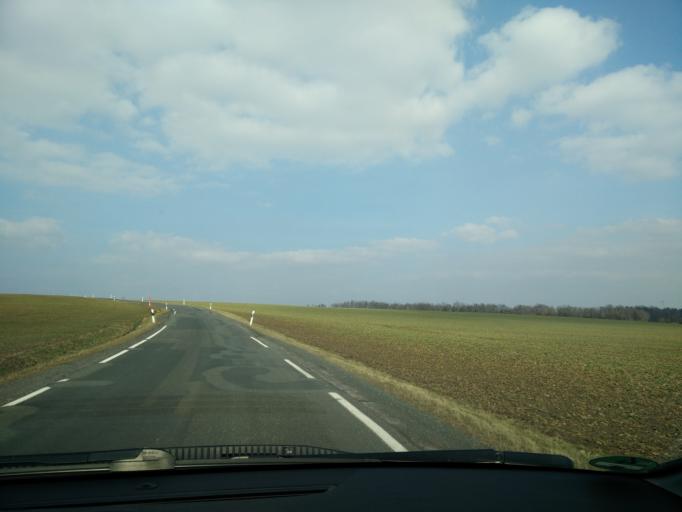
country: DE
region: Saxony
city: Colditz
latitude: 51.1066
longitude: 12.7751
